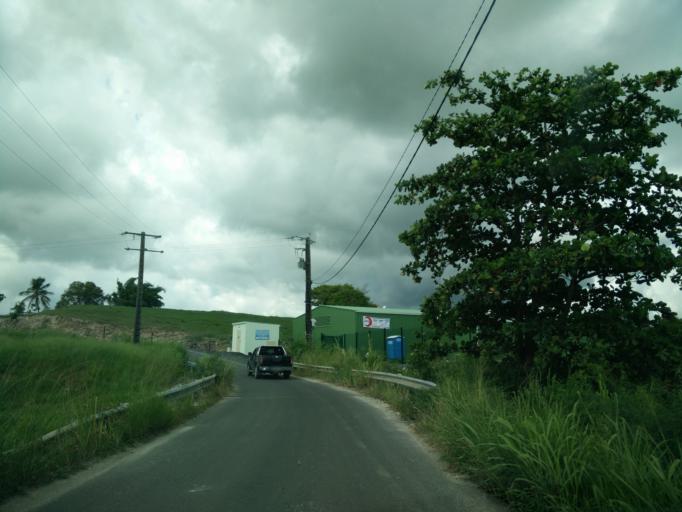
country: GP
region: Guadeloupe
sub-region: Guadeloupe
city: Le Moule
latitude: 16.3012
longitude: -61.3405
